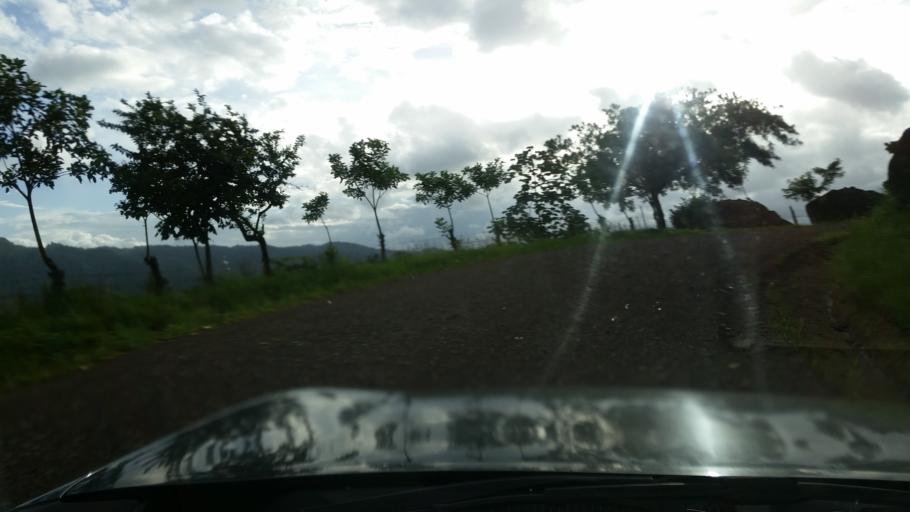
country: NI
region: Jinotega
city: Jinotega
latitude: 13.2504
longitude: -85.7361
